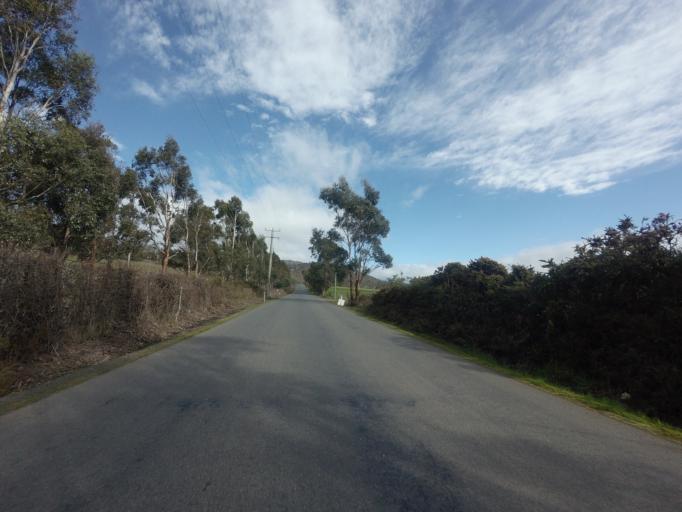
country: AU
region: Tasmania
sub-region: Derwent Valley
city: New Norfolk
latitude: -42.7817
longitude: 147.0028
